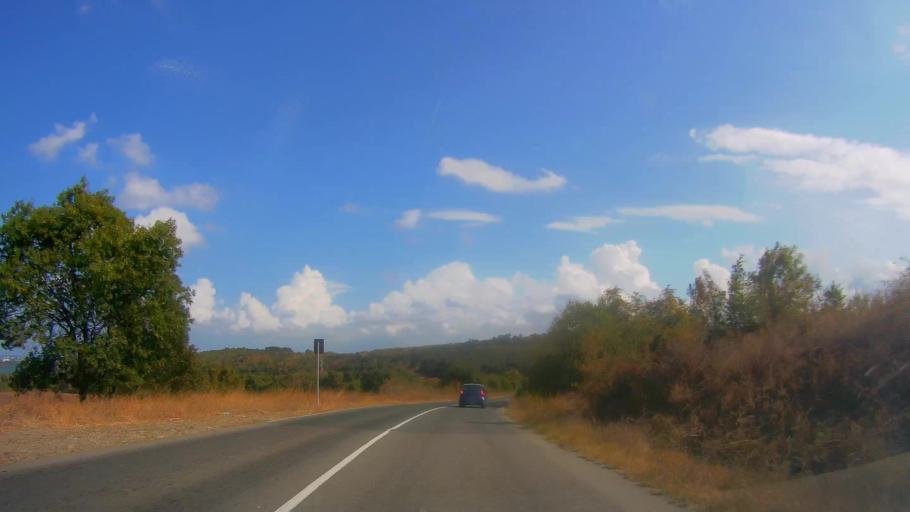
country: BG
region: Burgas
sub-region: Obshtina Burgas
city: Burgas
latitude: 42.4763
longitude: 27.3950
